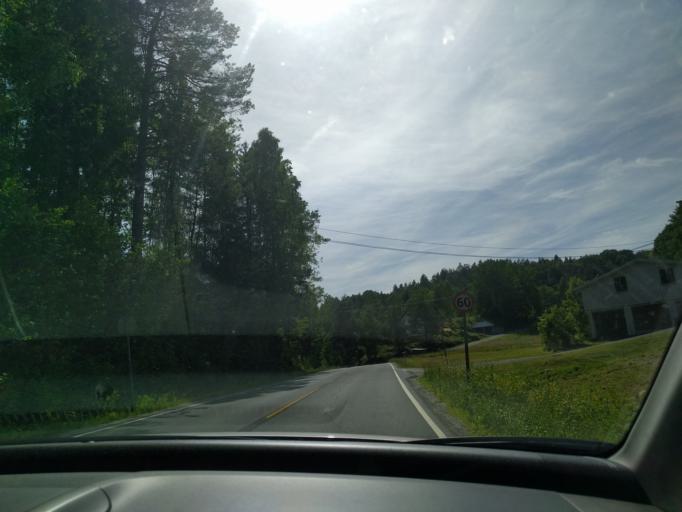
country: NO
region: Aust-Agder
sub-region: Gjerstad
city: Gjerstad
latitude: 58.8480
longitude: 9.0842
